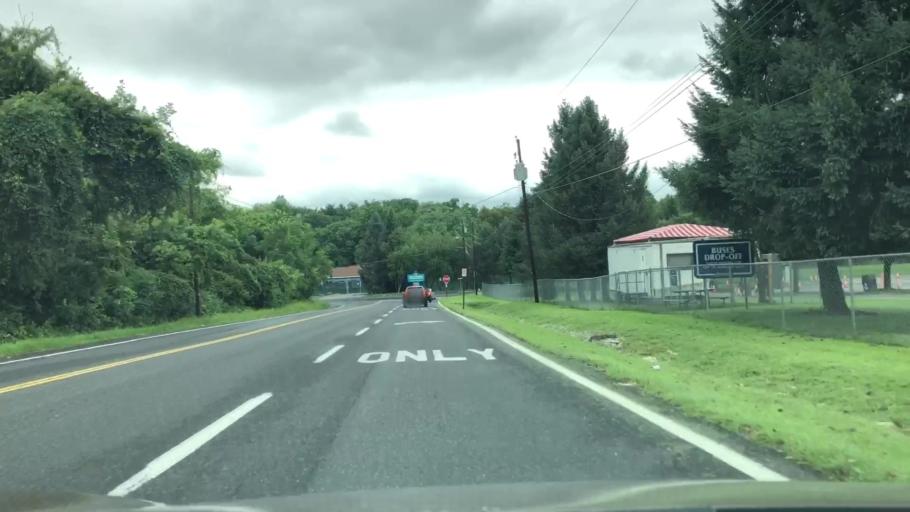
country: US
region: Pennsylvania
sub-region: Lehigh County
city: Dorneyville
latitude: 40.5761
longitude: -75.5360
